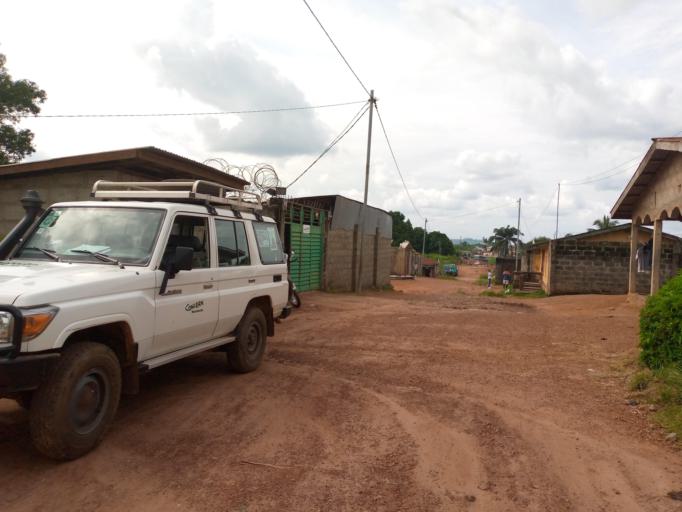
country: SL
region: Northern Province
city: Magburaka
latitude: 8.7231
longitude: -11.9407
